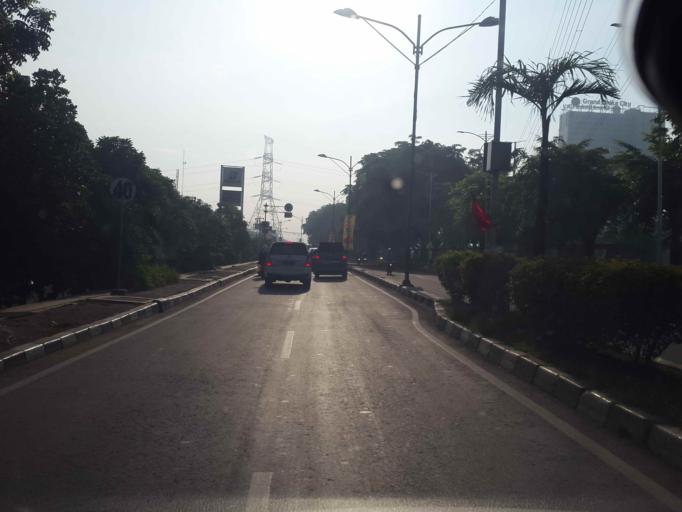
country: ID
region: West Java
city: Bekasi
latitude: -6.2601
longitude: 107.0166
